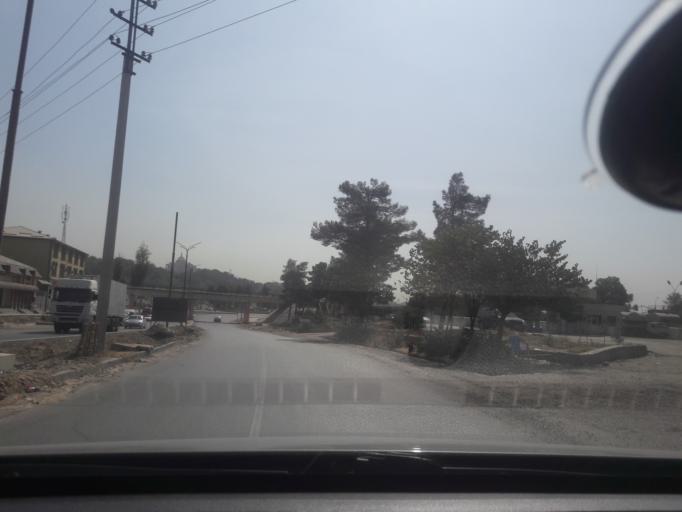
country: TJ
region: Dushanbe
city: Dushanbe
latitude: 38.6039
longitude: 68.7733
